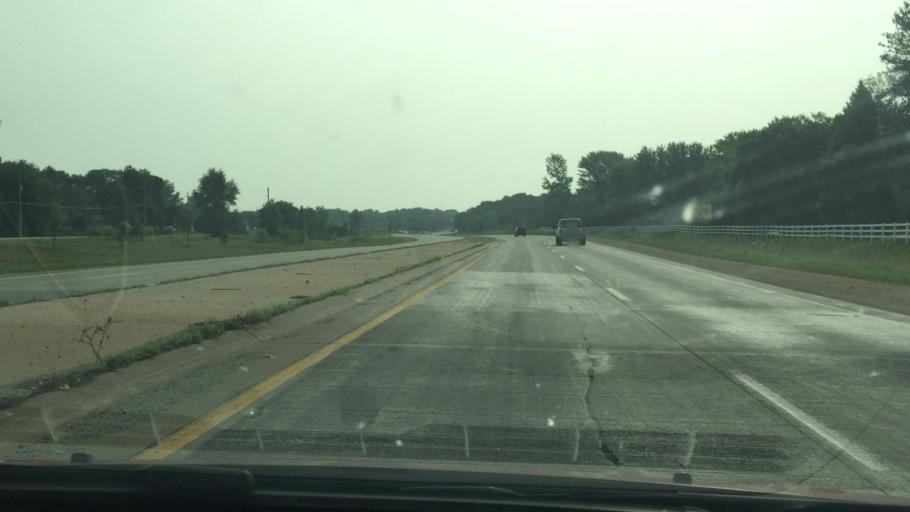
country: US
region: Iowa
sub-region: Scott County
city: Buffalo
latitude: 41.5085
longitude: -90.6822
